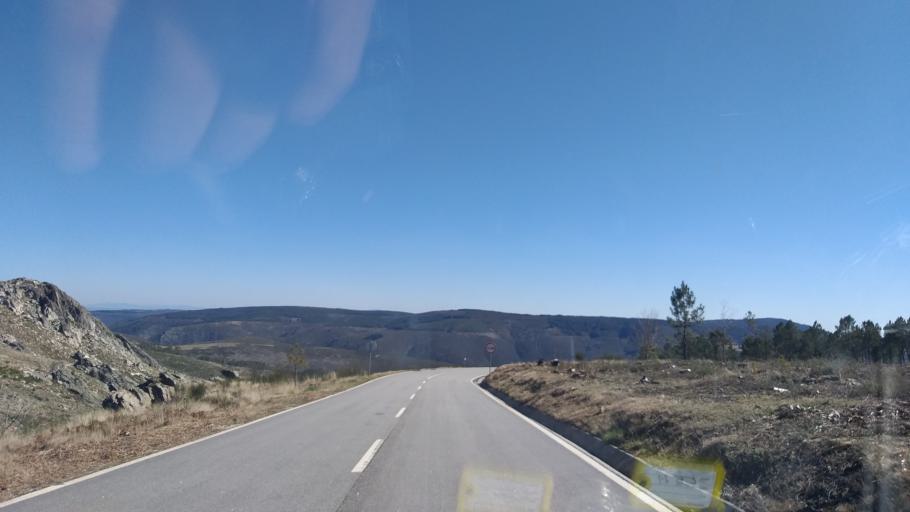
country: PT
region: Guarda
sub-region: Manteigas
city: Manteigas
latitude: 40.4780
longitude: -7.5083
